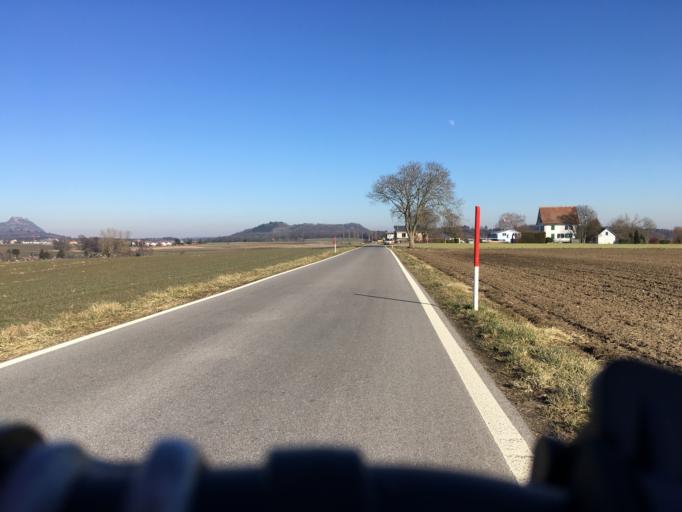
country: DE
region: Baden-Wuerttemberg
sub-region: Freiburg Region
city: Gottmadingen
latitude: 47.7169
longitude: 8.7741
